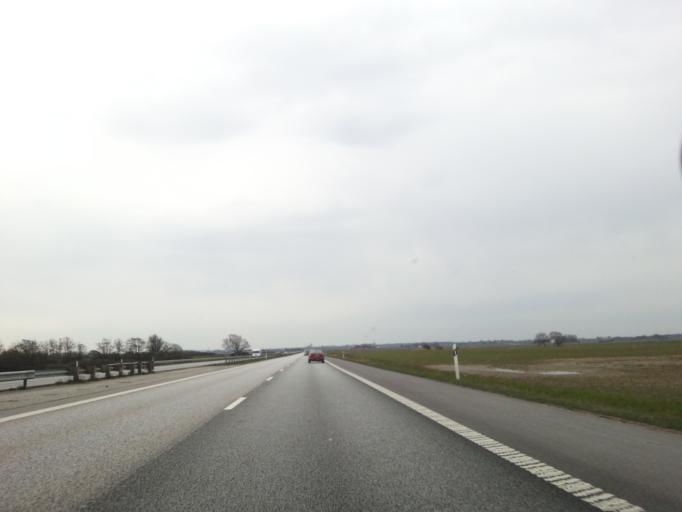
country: SE
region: Skane
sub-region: Angelholms Kommun
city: AEngelholm
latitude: 56.3017
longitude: 12.9068
